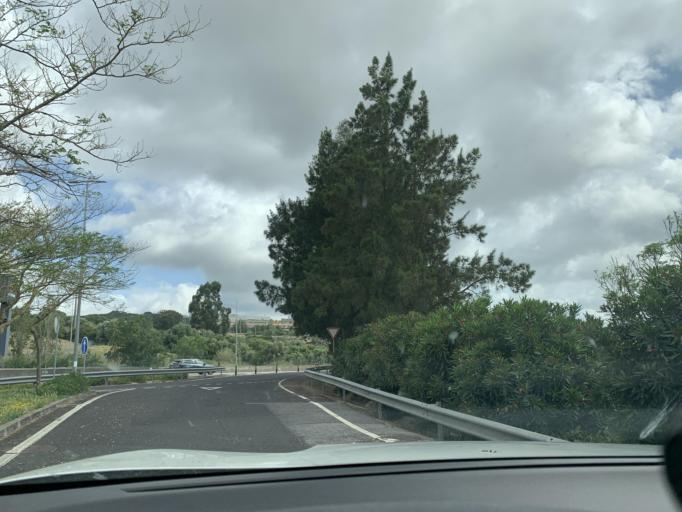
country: PT
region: Lisbon
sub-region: Loures
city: Santo Antao do Tojal
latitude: 38.8589
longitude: -9.1603
